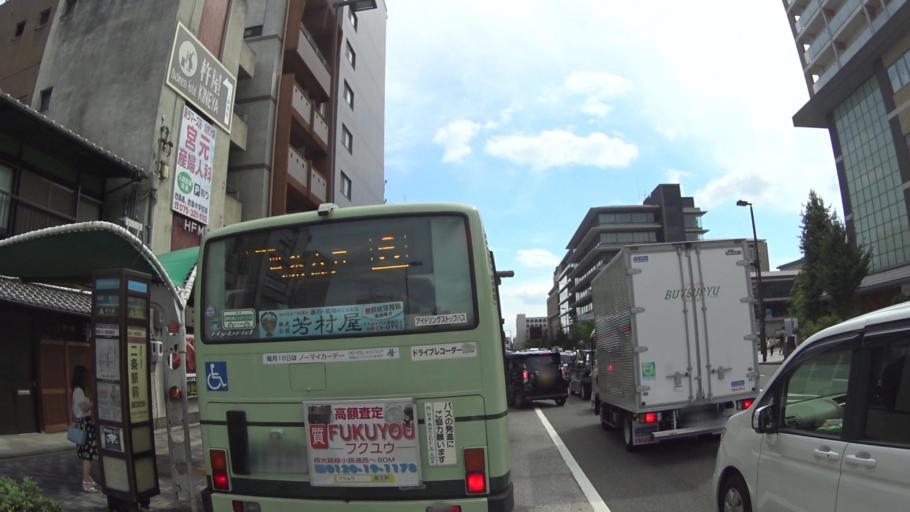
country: JP
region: Kyoto
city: Kyoto
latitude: 35.0119
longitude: 135.7425
